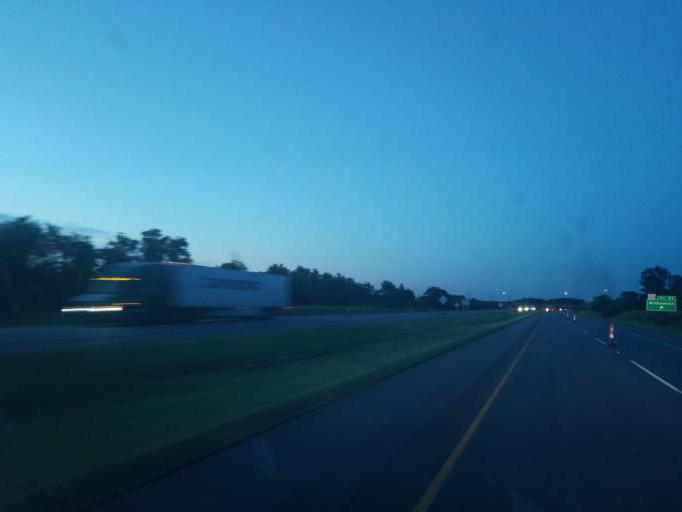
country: US
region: Indiana
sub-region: Saint Joseph County
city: Granger
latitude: 41.7261
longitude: -86.1516
